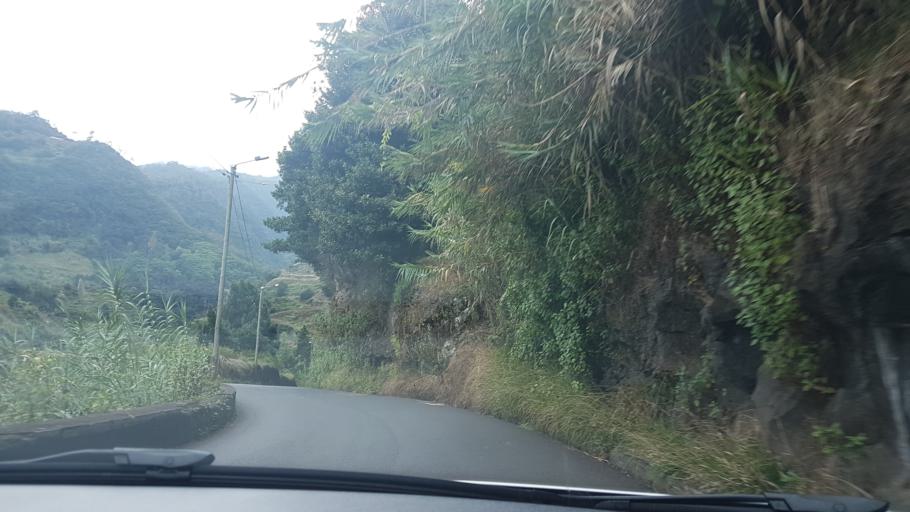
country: PT
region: Madeira
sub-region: Santana
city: Santana
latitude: 32.8223
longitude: -16.8996
